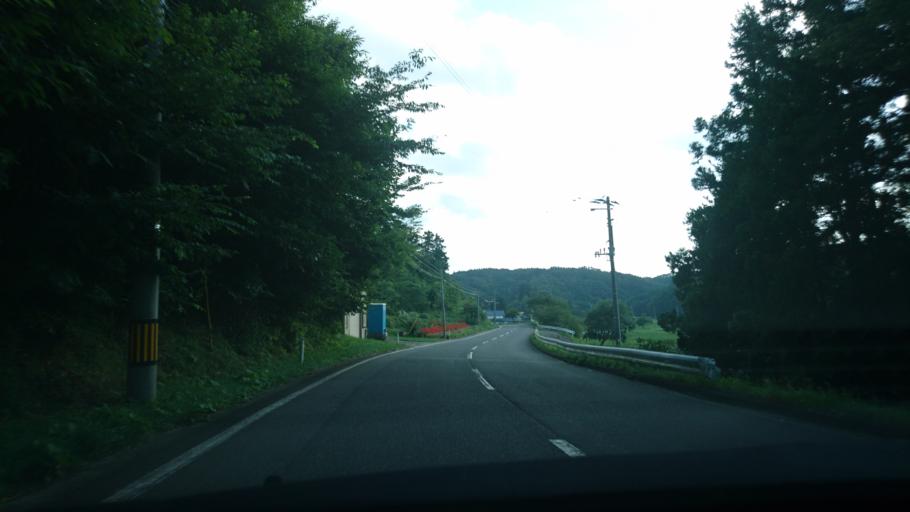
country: JP
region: Iwate
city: Ichinoseki
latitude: 39.0222
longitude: 141.2914
